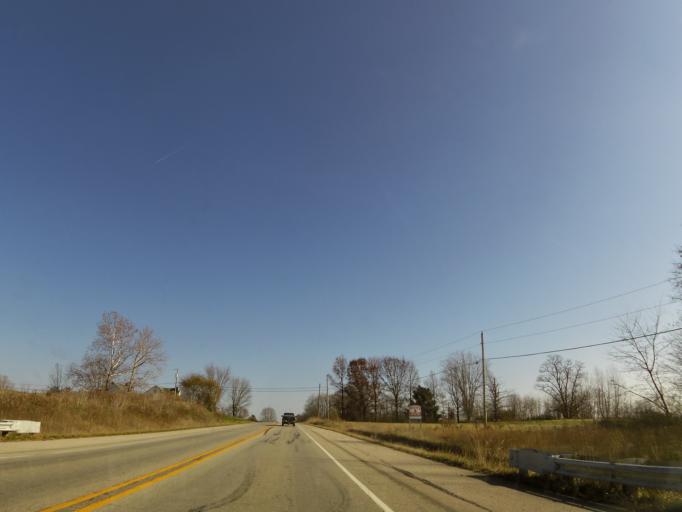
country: US
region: Indiana
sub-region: Fayette County
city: Connersville
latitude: 39.6354
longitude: -85.1971
